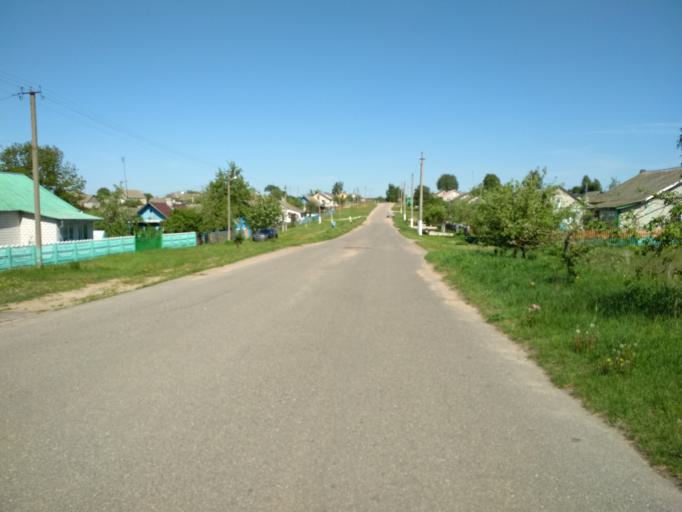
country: BY
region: Grodnenskaya
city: Mir
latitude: 53.3825
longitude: 26.3642
